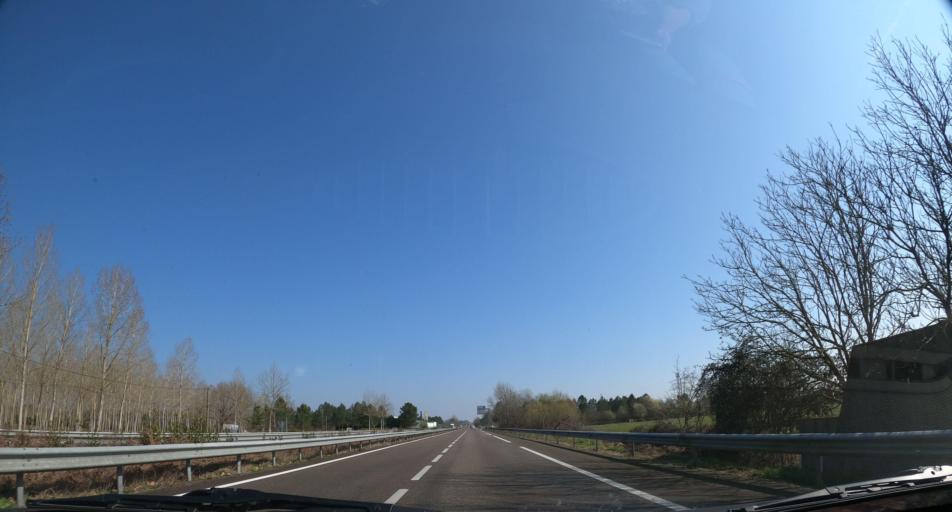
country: FR
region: Aquitaine
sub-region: Departement des Landes
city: Tartas
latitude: 43.8415
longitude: -0.7644
